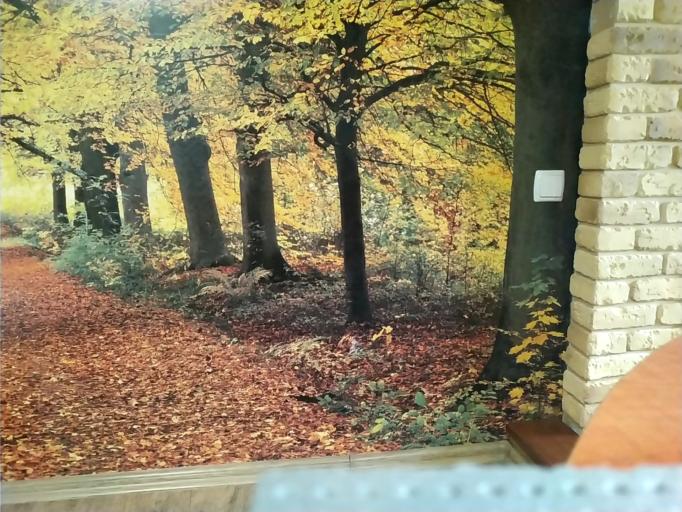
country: RU
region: Tverskaya
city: Staritsa
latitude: 56.4944
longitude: 35.2358
